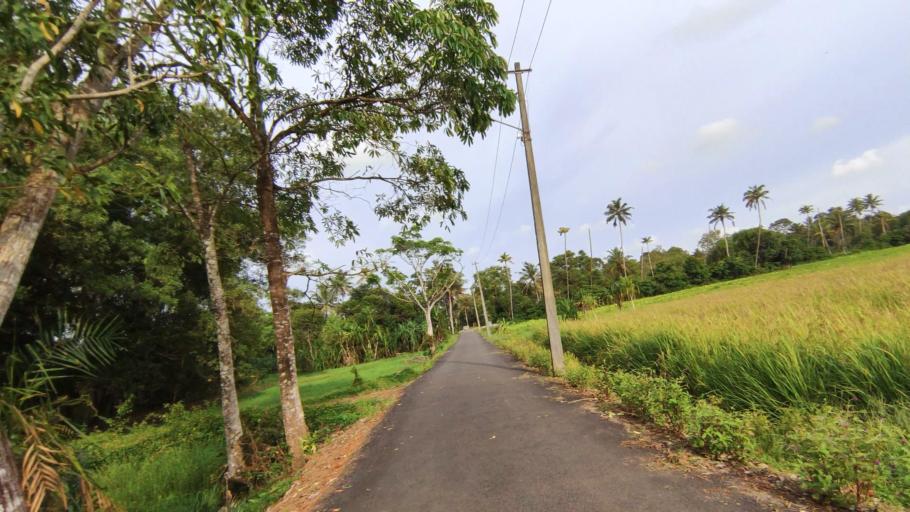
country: IN
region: Kerala
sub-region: Alappuzha
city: Shertallai
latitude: 9.6238
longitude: 76.3361
